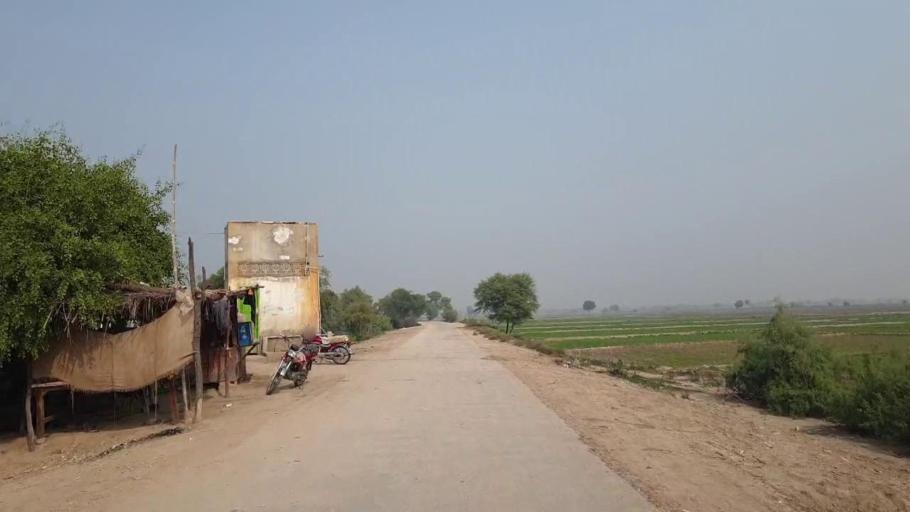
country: PK
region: Sindh
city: Bhan
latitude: 26.5240
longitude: 67.6916
